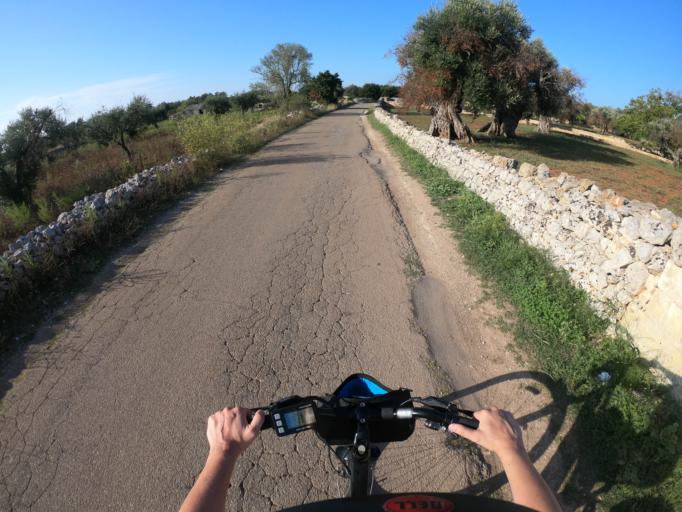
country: IT
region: Apulia
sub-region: Provincia di Lecce
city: Castrignano del Capo
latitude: 39.8232
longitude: 18.3557
